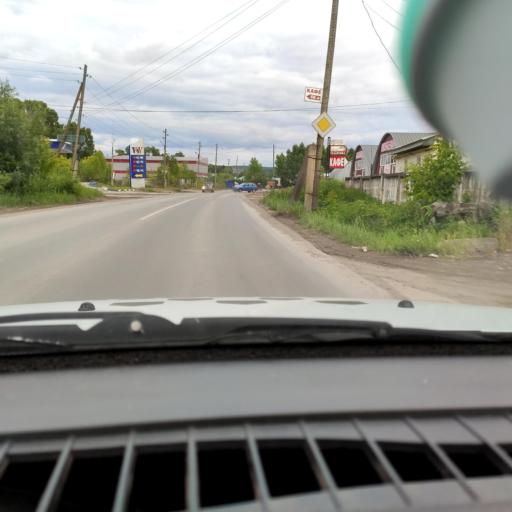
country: RU
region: Perm
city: Chusovoy
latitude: 58.3005
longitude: 57.8124
